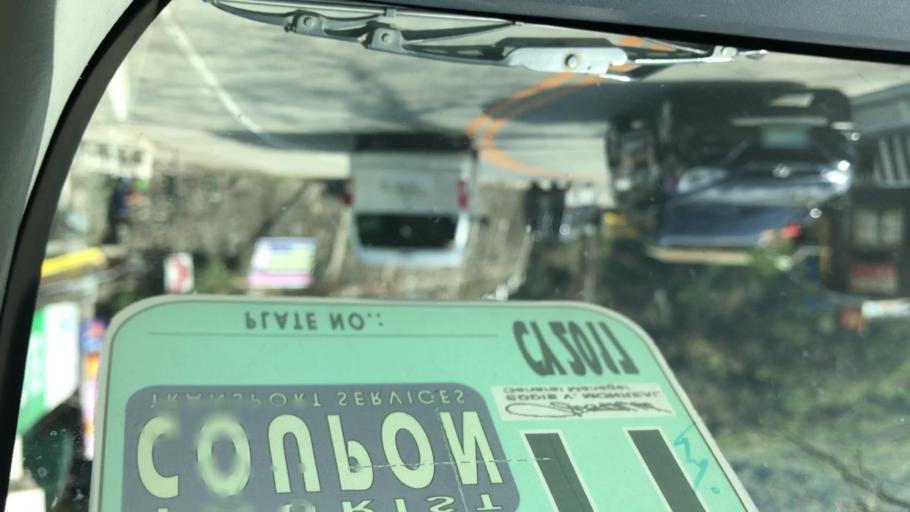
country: PH
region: Cordillera
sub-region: Province of Benguet
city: Tuba
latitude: 16.3107
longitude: 120.6169
